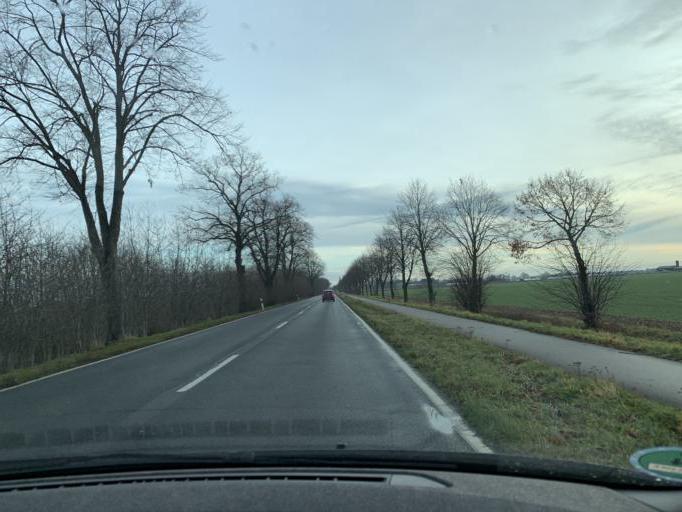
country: DE
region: North Rhine-Westphalia
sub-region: Regierungsbezirk Koln
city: Merzenich
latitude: 50.8118
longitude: 6.5652
